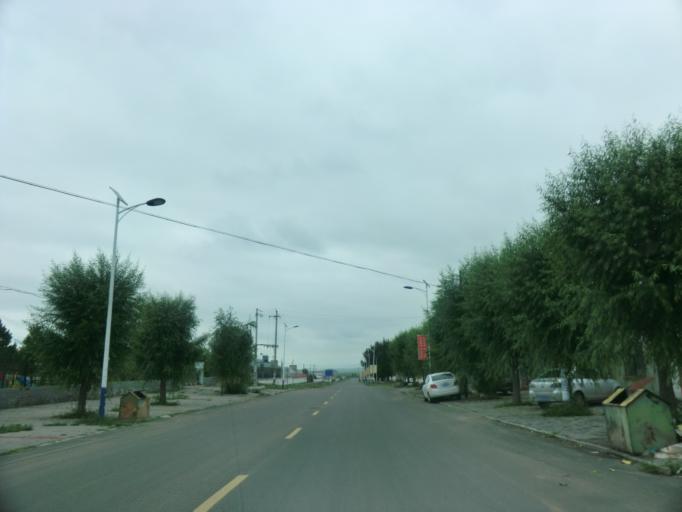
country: CN
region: Inner Mongolia
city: Bayart Huxu
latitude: 45.0906
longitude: 120.2440
